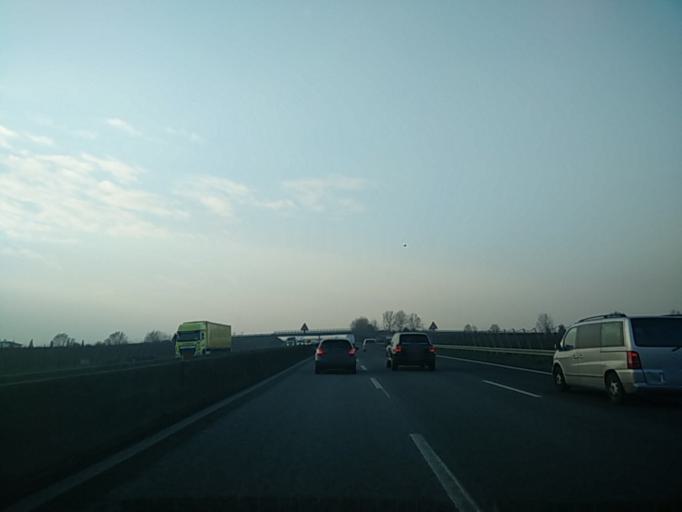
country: IT
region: Emilia-Romagna
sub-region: Provincia di Bologna
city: Mordano
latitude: 44.3690
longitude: 11.7748
